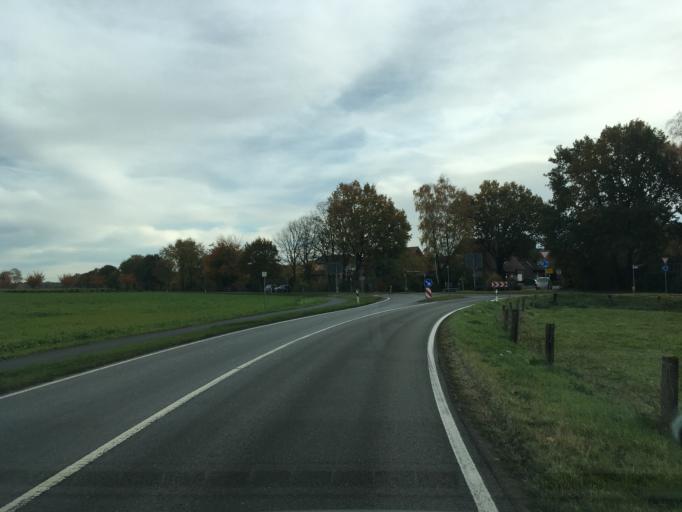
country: DE
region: North Rhine-Westphalia
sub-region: Regierungsbezirk Munster
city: Heiden
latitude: 51.8322
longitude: 6.9274
